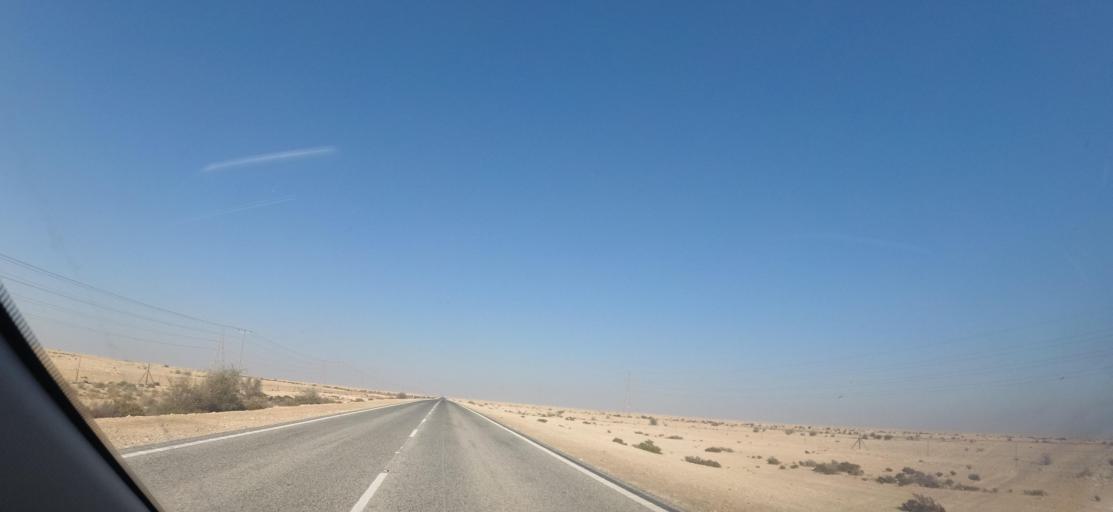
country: QA
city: Al Jumayliyah
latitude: 25.6846
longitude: 51.1394
